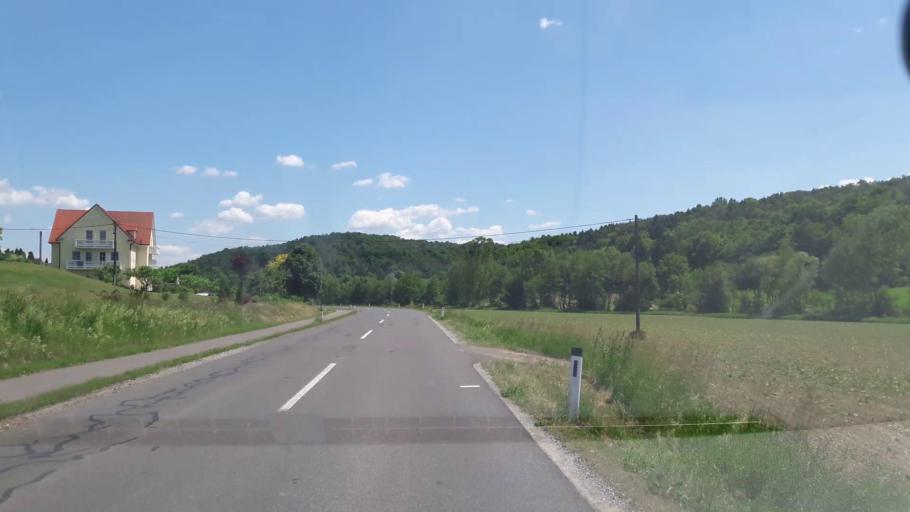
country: AT
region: Styria
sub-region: Politischer Bezirk Suedoststeiermark
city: Unterlamm
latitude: 46.9633
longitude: 16.0924
